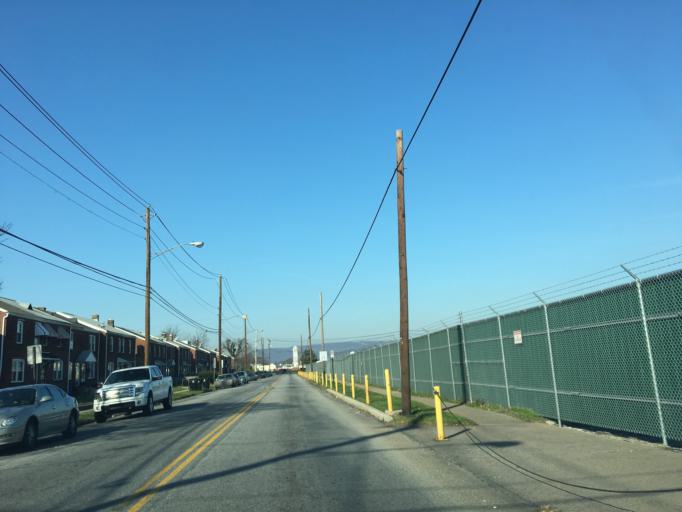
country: US
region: Pennsylvania
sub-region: Dauphin County
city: Harrisburg
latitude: 40.2898
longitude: -76.8913
